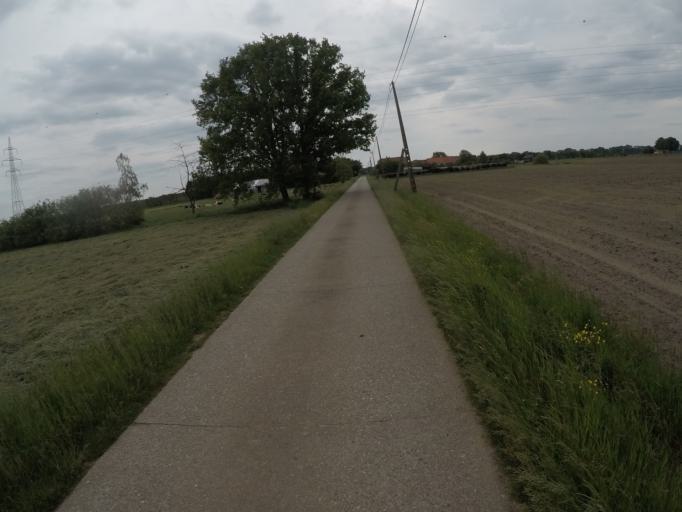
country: BE
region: Flanders
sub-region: Provincie Antwerpen
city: Oostmalle
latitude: 51.3292
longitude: 4.6913
